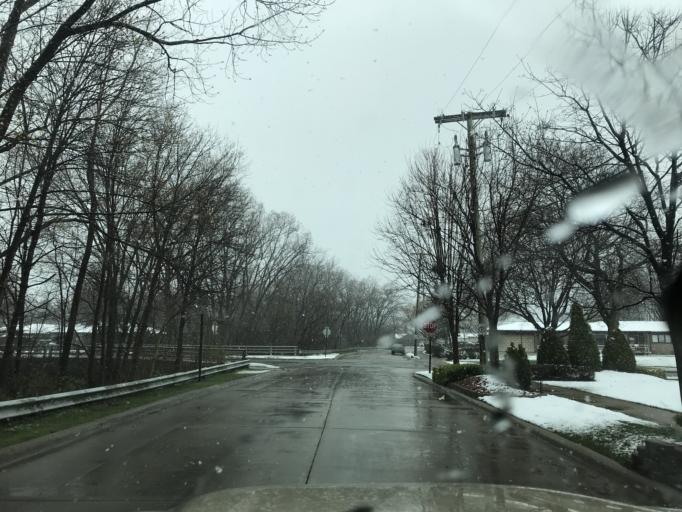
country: US
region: Michigan
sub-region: Wayne County
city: Allen Park
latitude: 42.2334
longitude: -83.2191
